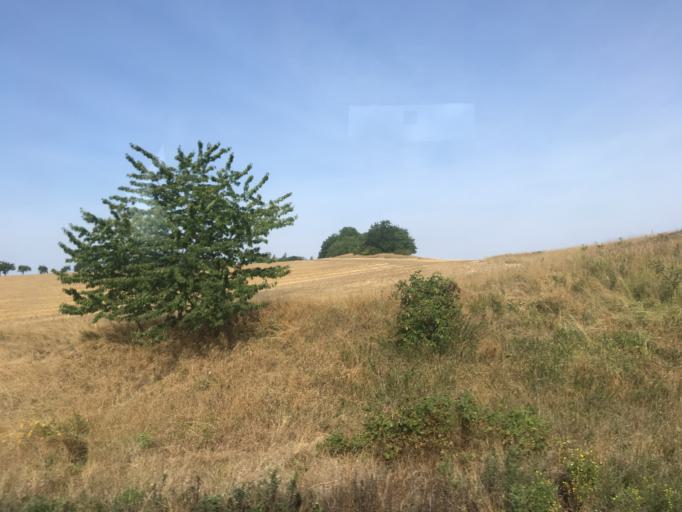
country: CZ
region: Central Bohemia
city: Votice
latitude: 49.6757
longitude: 14.6274
